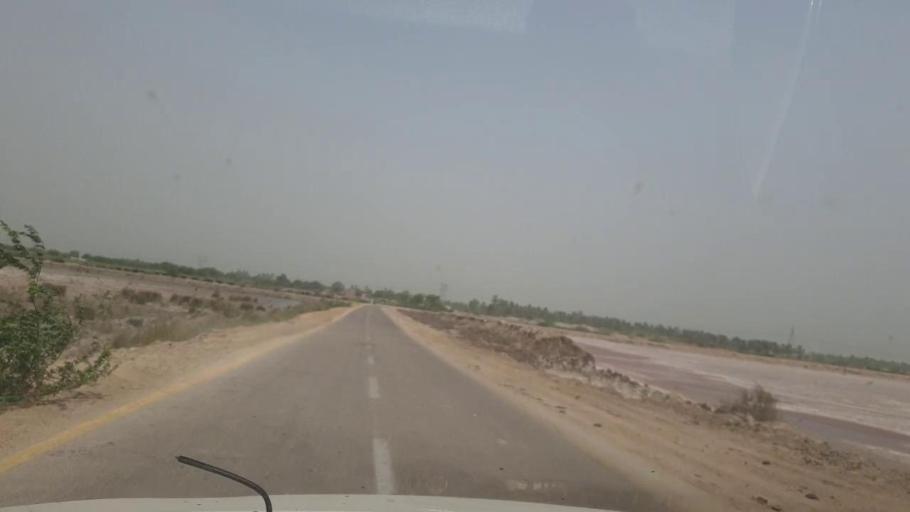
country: PK
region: Sindh
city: Kot Diji
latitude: 27.4021
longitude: 68.6593
